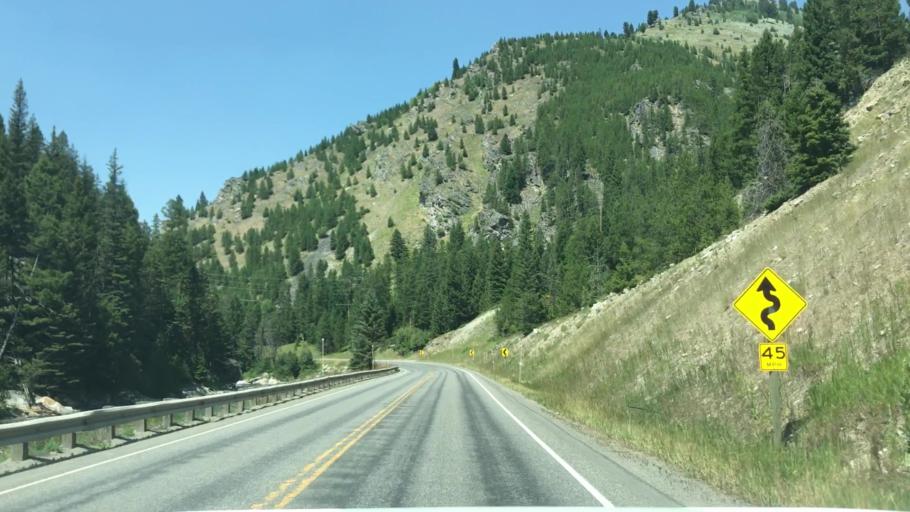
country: US
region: Montana
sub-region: Gallatin County
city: Big Sky
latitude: 45.3886
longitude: -111.1974
